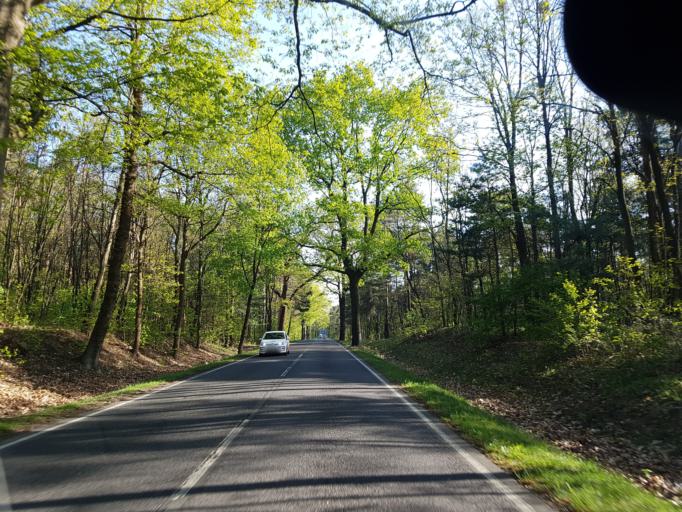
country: DE
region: Brandenburg
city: Grossraschen
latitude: 51.6182
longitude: 14.0238
